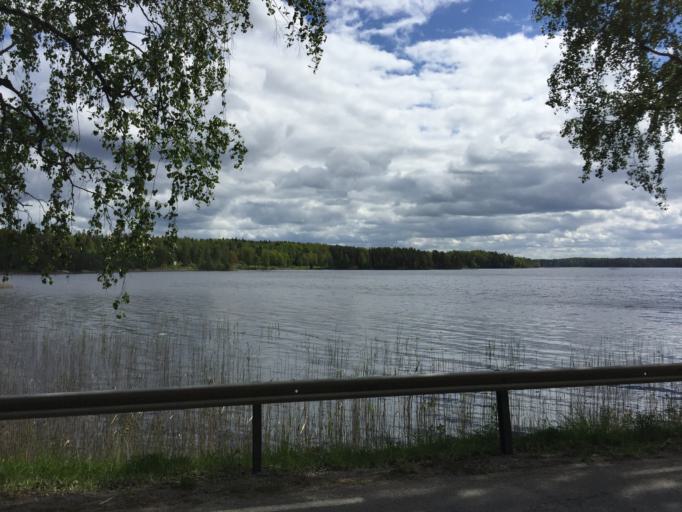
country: SE
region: Soedermanland
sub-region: Vingakers Kommun
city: Vingaker
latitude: 58.9326
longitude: 15.6742
